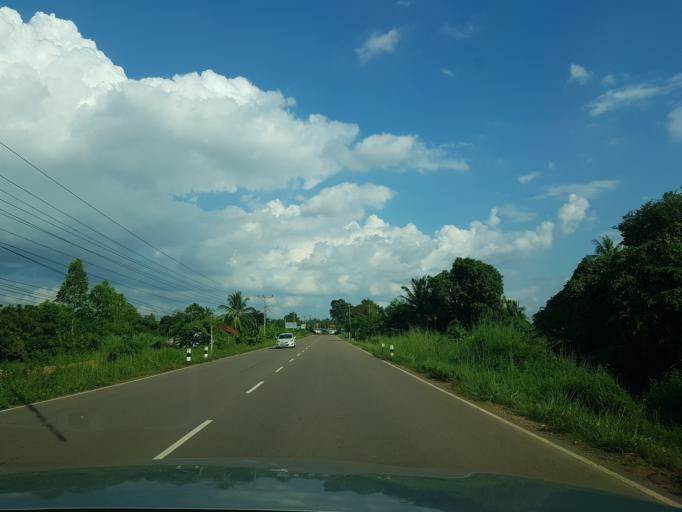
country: TH
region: Nong Khai
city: Pho Tak
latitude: 17.9800
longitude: 102.4600
